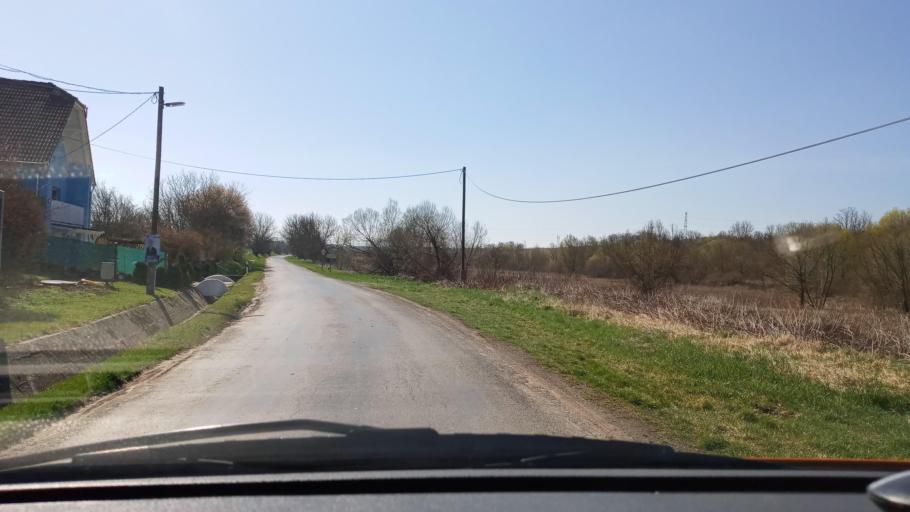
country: HU
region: Baranya
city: Kozarmisleny
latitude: 46.0551
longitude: 18.3773
